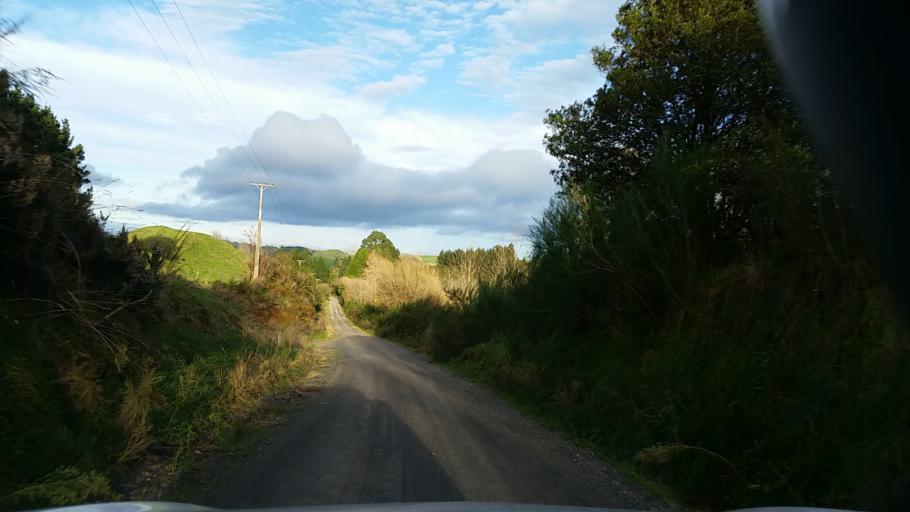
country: NZ
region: Bay of Plenty
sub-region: Rotorua District
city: Rotorua
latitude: -38.2983
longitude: 176.2770
